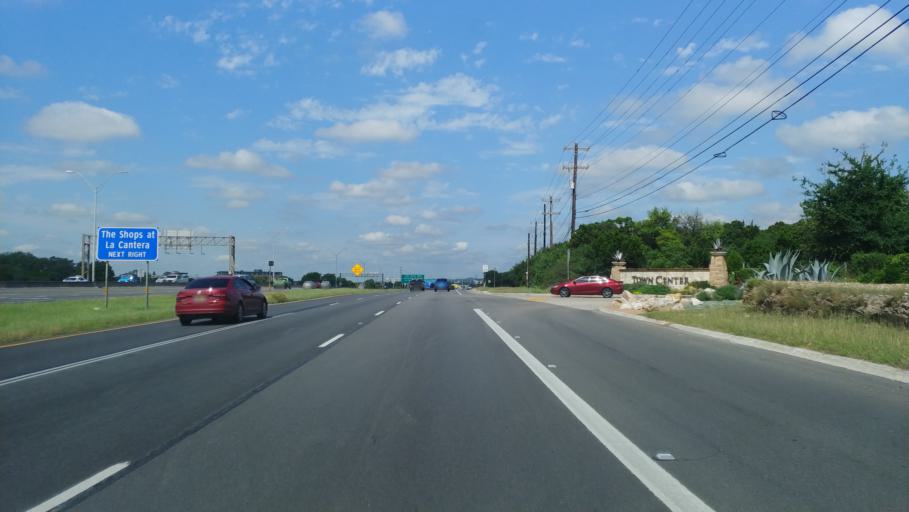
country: US
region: Texas
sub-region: Bexar County
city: Shavano Park
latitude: 29.5902
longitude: -98.6077
